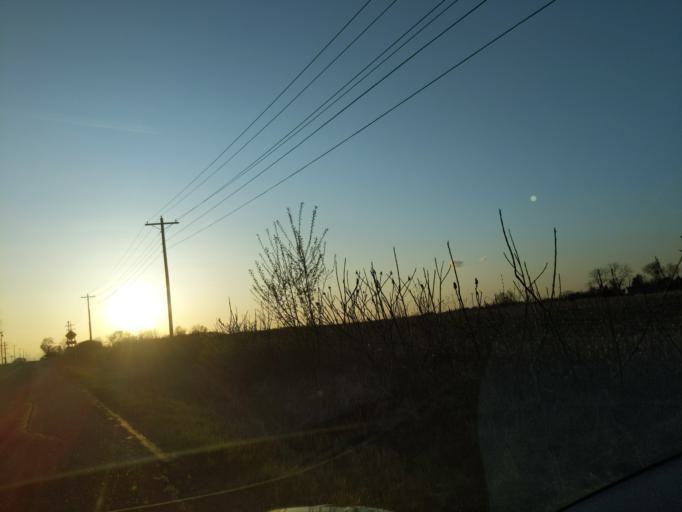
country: US
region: Michigan
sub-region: Ingham County
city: Leslie
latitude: 42.5095
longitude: -84.4502
